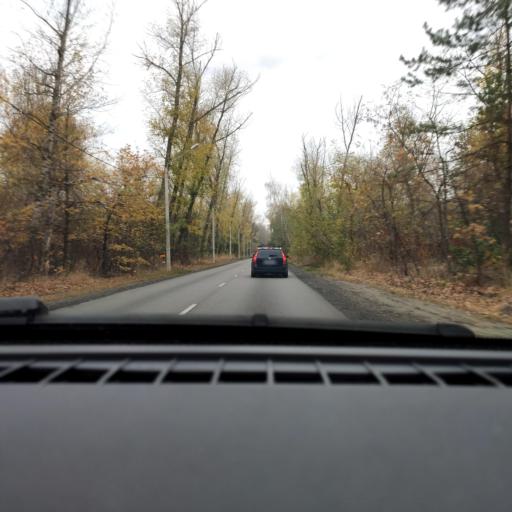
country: RU
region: Voronezj
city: Somovo
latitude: 51.7203
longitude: 39.3213
